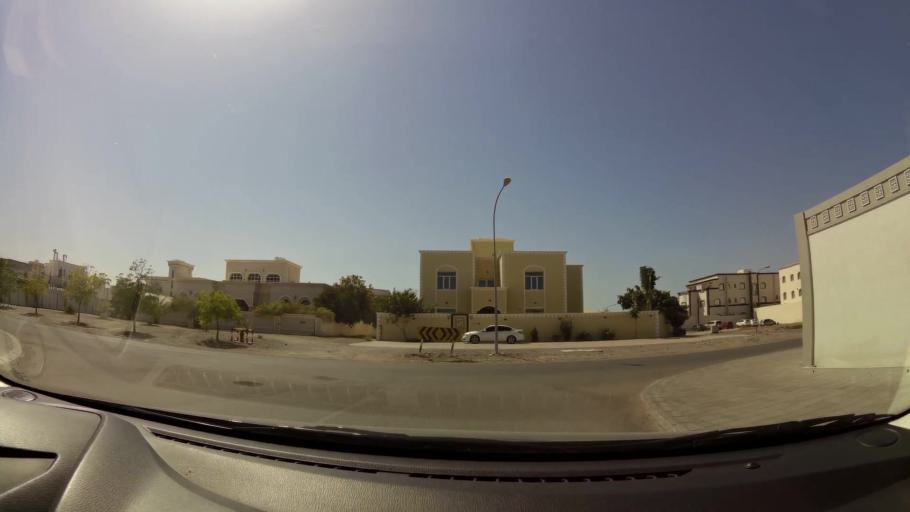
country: OM
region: Muhafazat Masqat
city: As Sib al Jadidah
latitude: 23.6345
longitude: 58.2170
